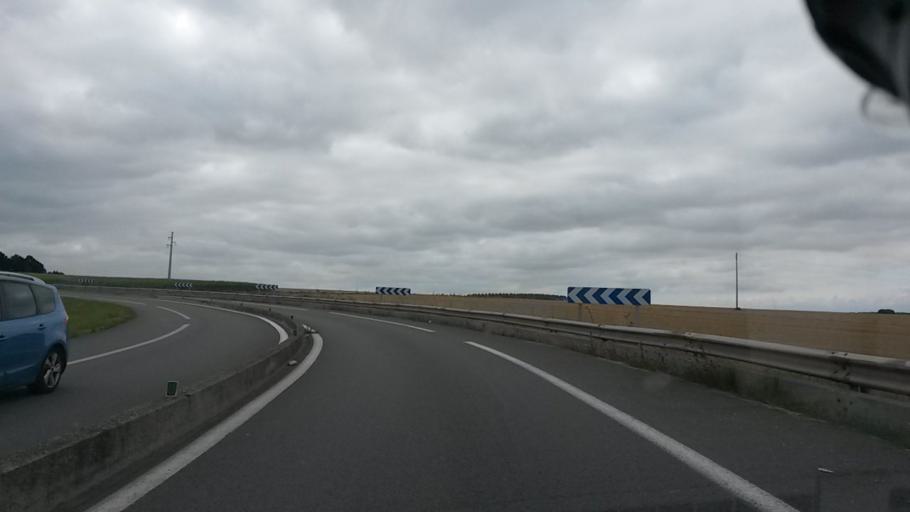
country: FR
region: Nord-Pas-de-Calais
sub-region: Departement du Nord
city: Raillencourt-Sainte-Olle
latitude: 50.1799
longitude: 3.1848
